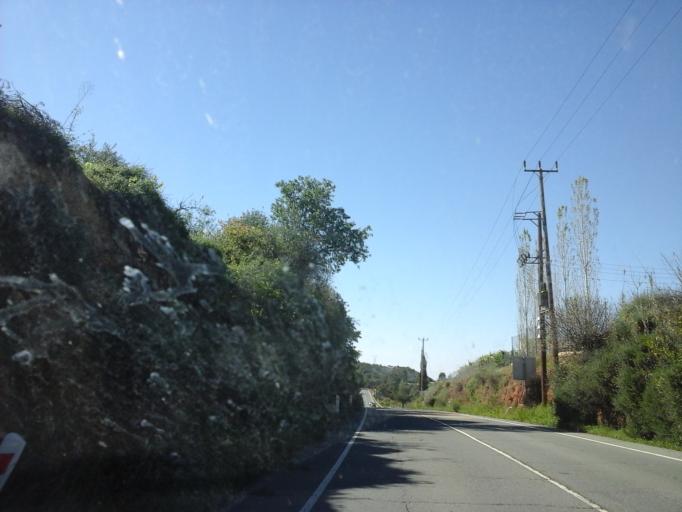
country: CY
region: Limassol
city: Sotira
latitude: 34.7981
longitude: 32.9150
